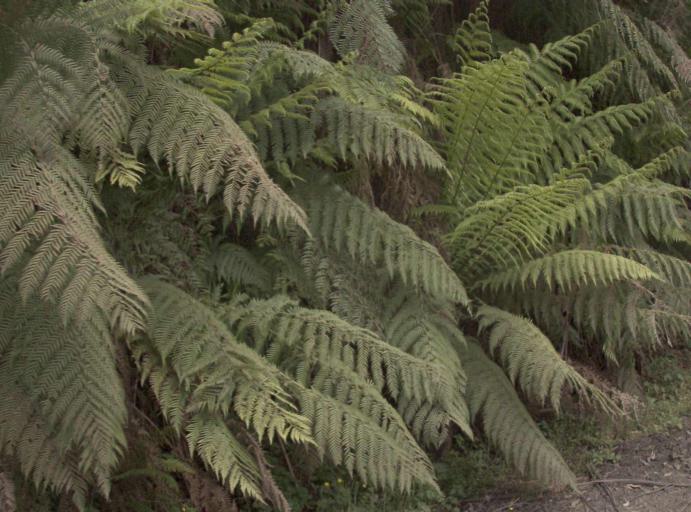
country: AU
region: Victoria
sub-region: Latrobe
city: Traralgon
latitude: -38.4236
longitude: 146.5676
